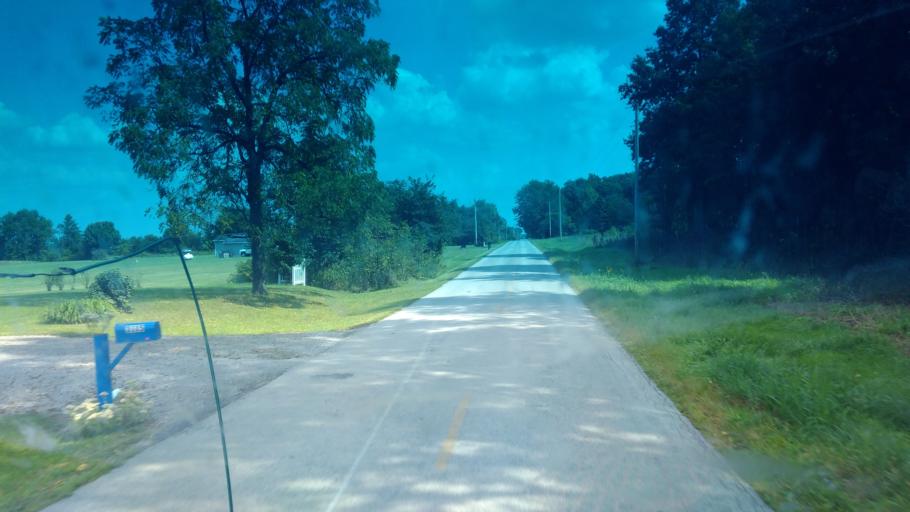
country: US
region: Ohio
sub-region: Hardin County
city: Ada
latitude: 40.7186
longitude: -83.8207
